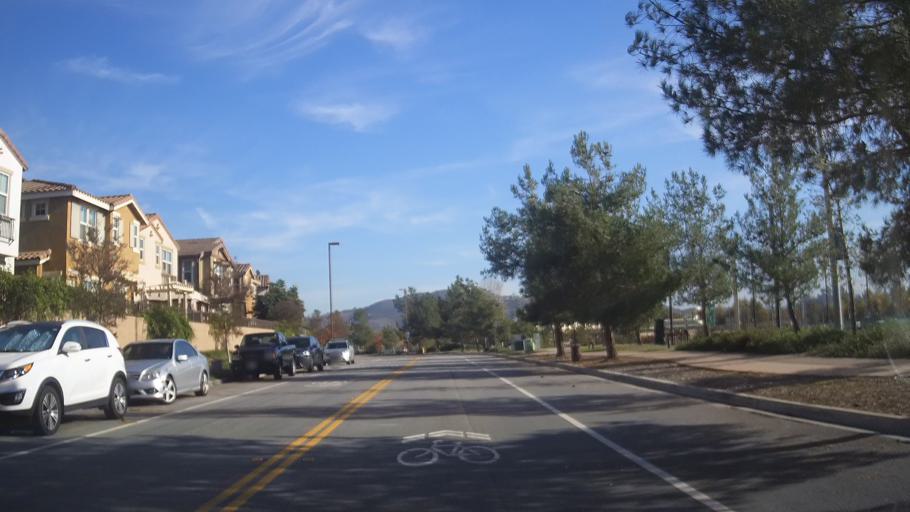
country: US
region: California
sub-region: San Diego County
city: Santee
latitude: 32.8522
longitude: -116.9798
